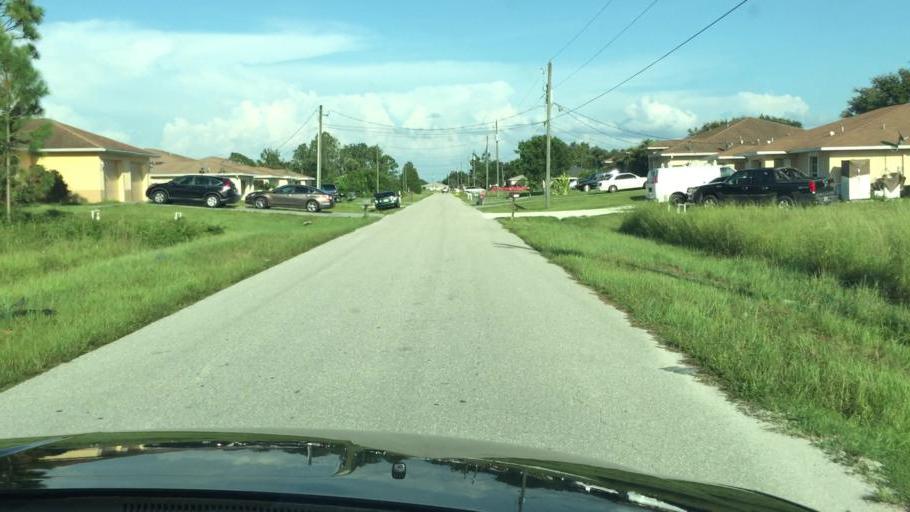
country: US
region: Florida
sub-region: Lee County
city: Gateway
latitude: 26.5906
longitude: -81.7209
